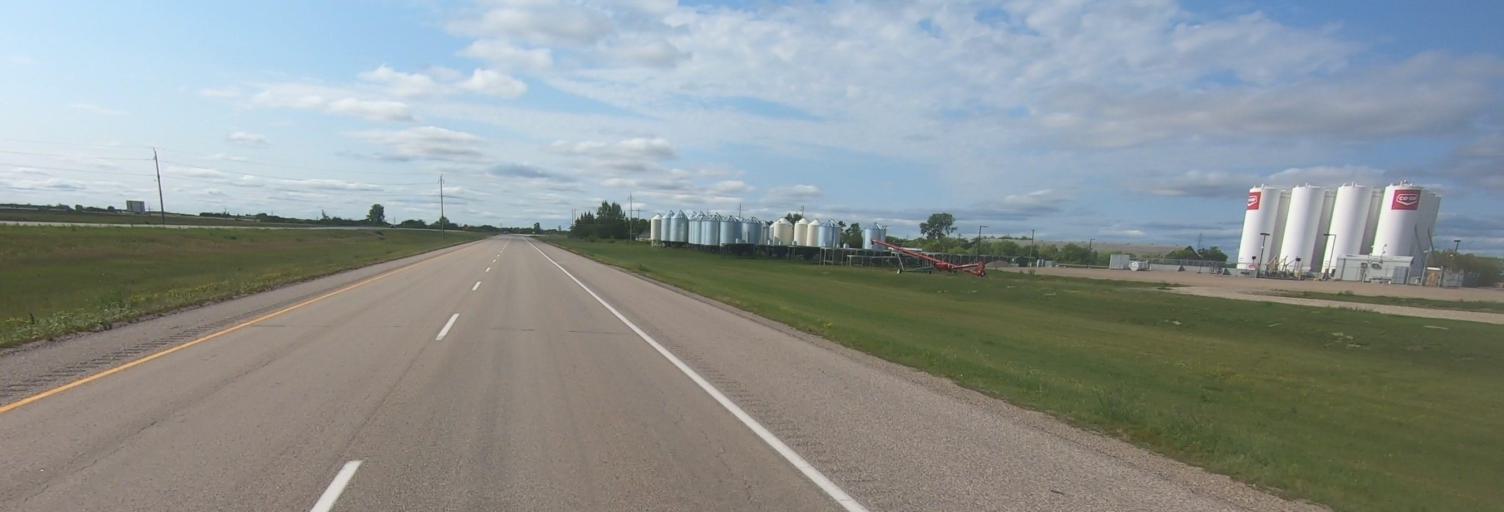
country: CA
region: Manitoba
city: Virden
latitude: 49.8699
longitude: -100.9596
